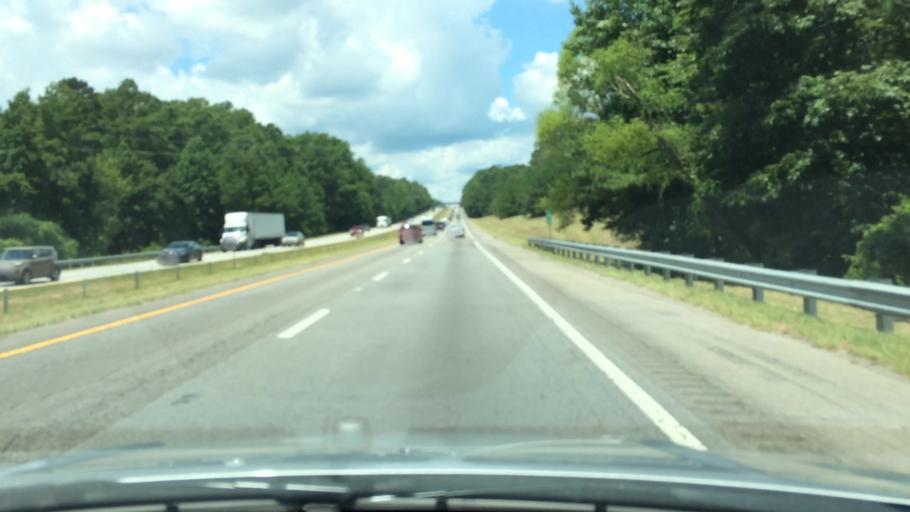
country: US
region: South Carolina
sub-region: Lexington County
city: Chapin
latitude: 34.1872
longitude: -81.3394
